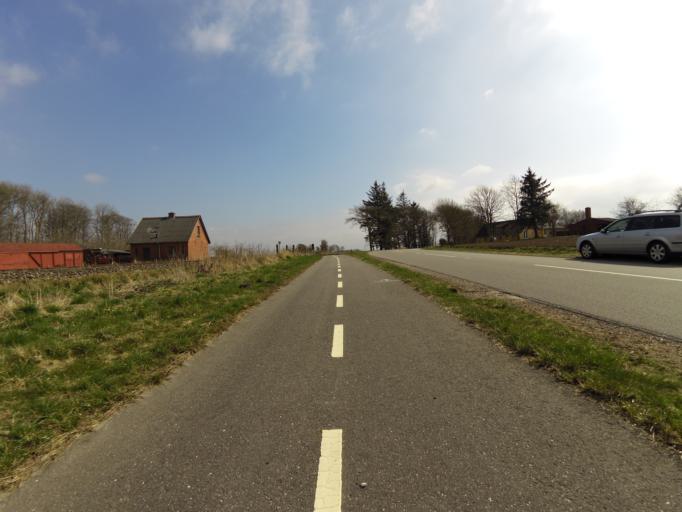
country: DK
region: Central Jutland
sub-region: Struer Kommune
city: Struer
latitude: 56.4500
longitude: 8.6211
